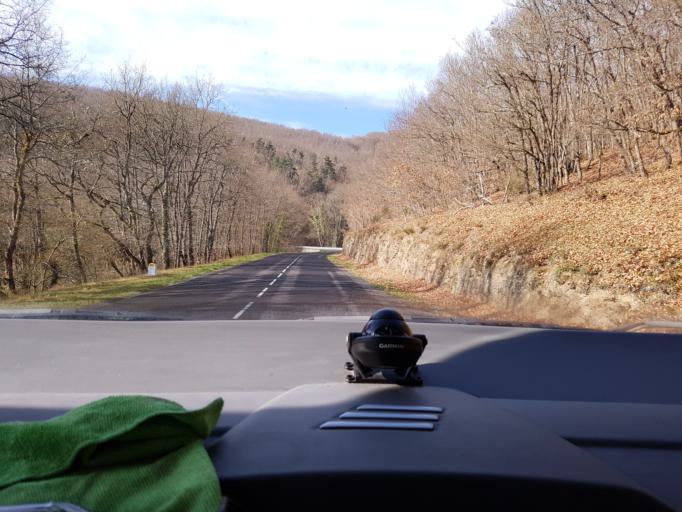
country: FR
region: Auvergne
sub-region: Departement du Cantal
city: Massiac
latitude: 45.2380
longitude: 3.2009
